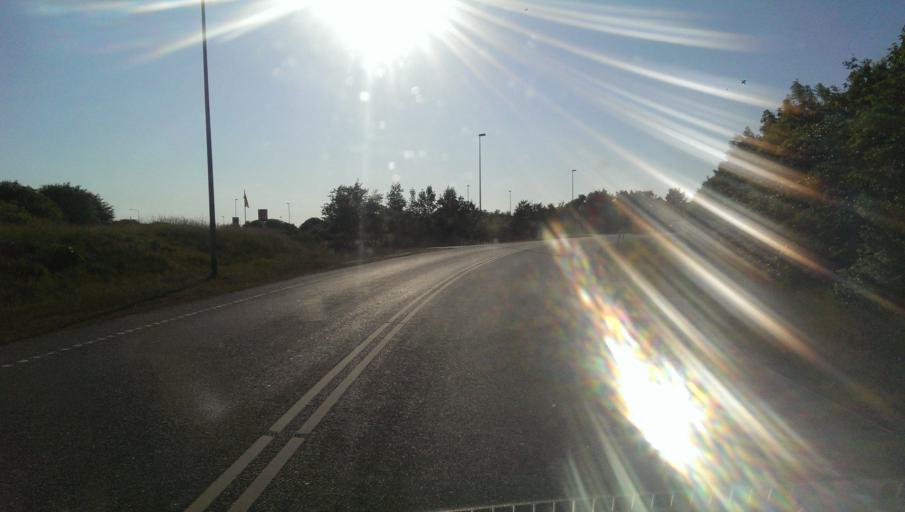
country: DK
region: South Denmark
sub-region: Esbjerg Kommune
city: Tjaereborg
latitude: 55.5249
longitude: 8.5950
